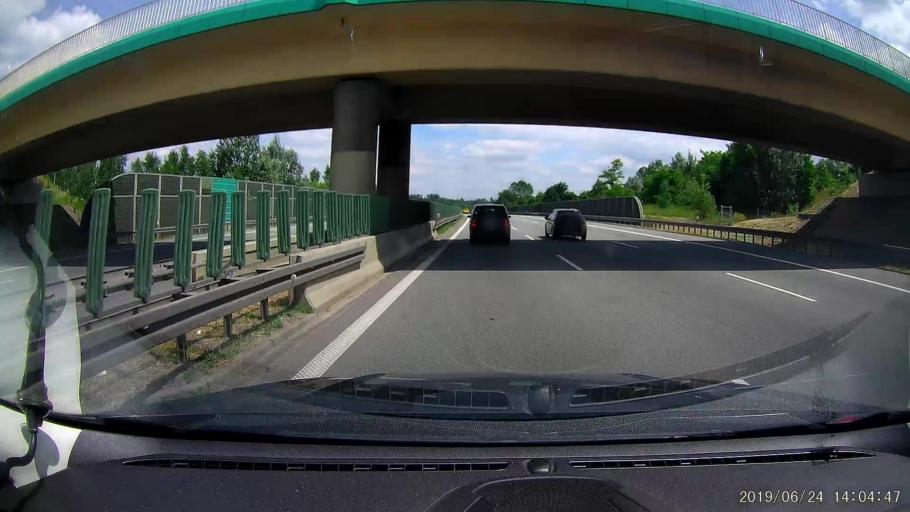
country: PL
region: Lesser Poland Voivodeship
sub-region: Powiat krakowski
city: Wrzasowice
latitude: 50.0004
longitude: 19.9577
